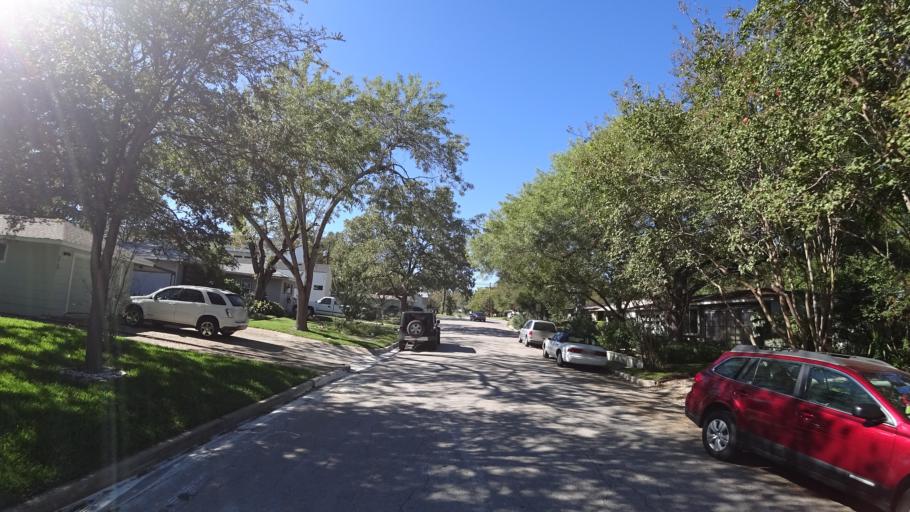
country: US
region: Texas
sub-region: Travis County
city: Austin
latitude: 30.3255
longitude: -97.7498
